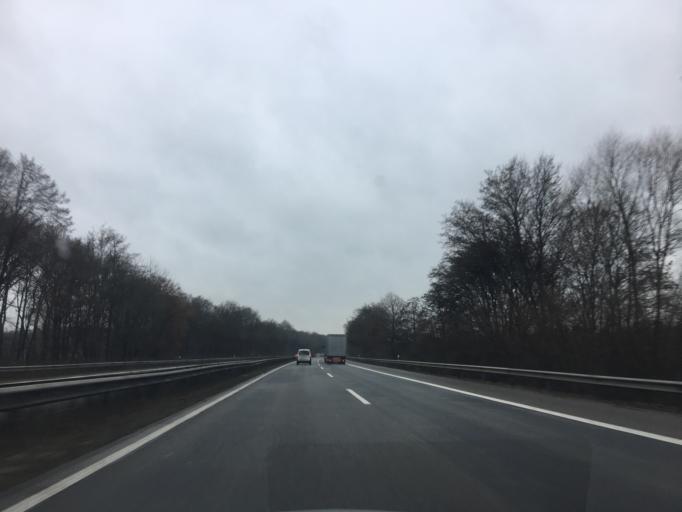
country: DE
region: North Rhine-Westphalia
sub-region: Regierungsbezirk Dusseldorf
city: Kaarst
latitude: 51.2340
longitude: 6.5858
